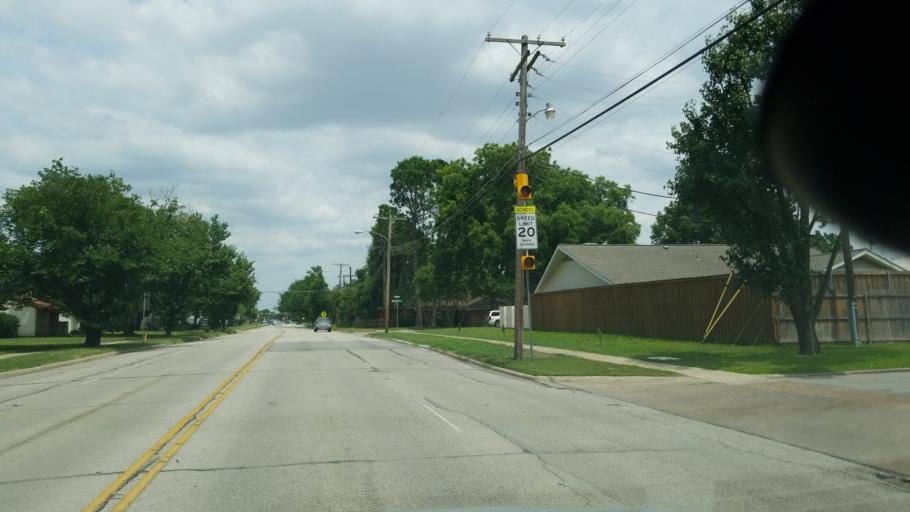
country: US
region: Texas
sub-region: Dallas County
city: Irving
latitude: 32.8442
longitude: -96.9563
